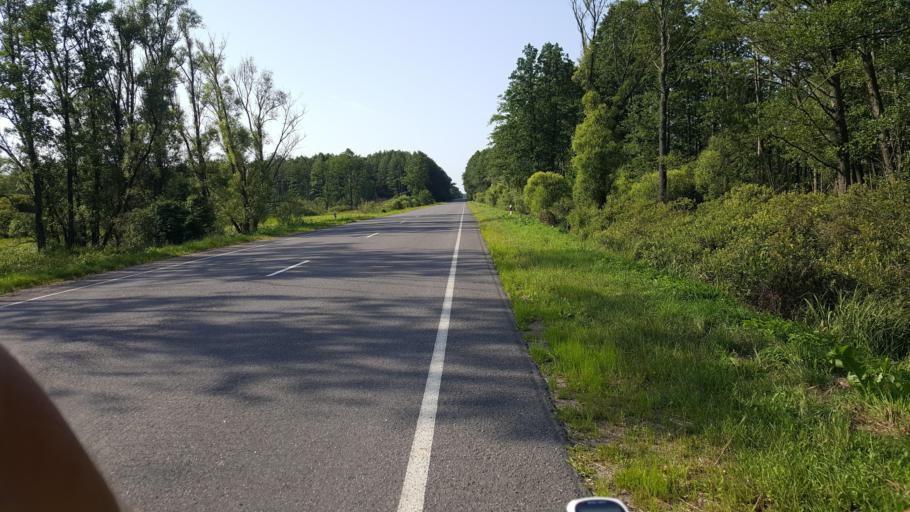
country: BY
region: Brest
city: Zhabinka
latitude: 52.2799
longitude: 23.9490
